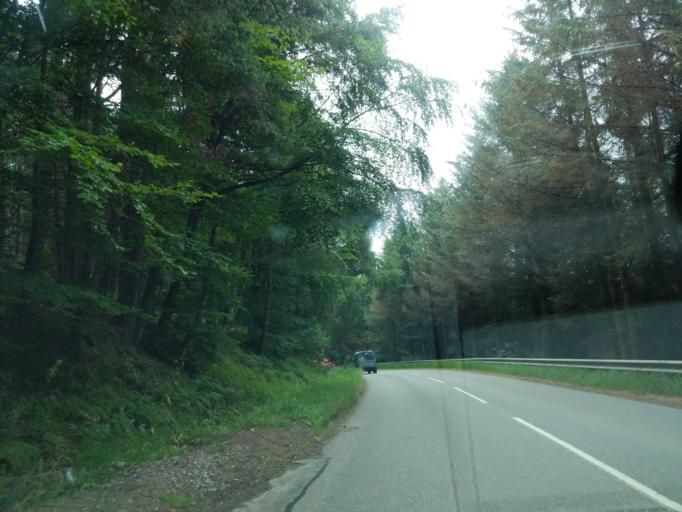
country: GB
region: Scotland
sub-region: Moray
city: Rothes
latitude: 57.4923
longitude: -3.1938
